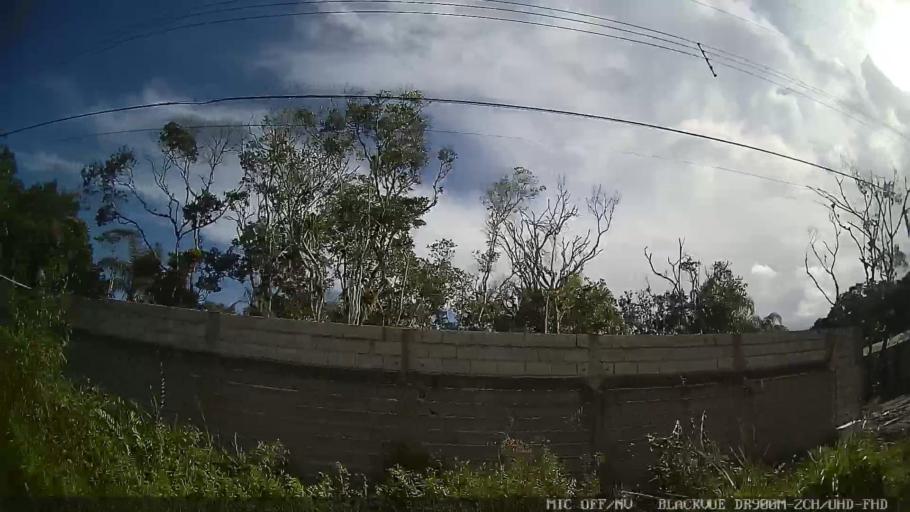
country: BR
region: Sao Paulo
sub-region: Itanhaem
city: Itanhaem
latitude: -24.2045
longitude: -46.8858
